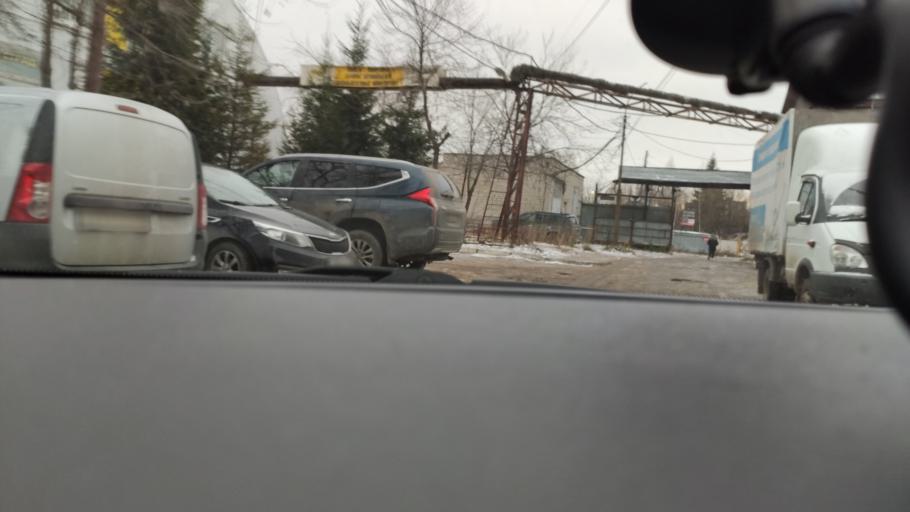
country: RU
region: Perm
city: Perm
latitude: 57.9845
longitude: 56.2759
